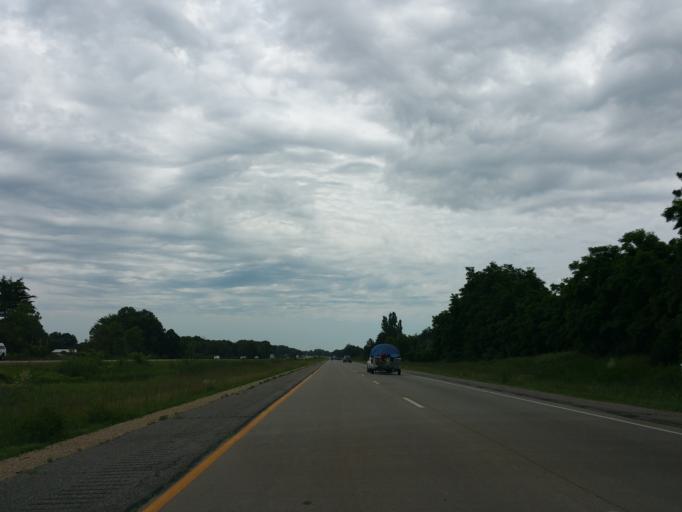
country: US
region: Wisconsin
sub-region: Juneau County
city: Mauston
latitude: 43.8352
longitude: -90.0918
